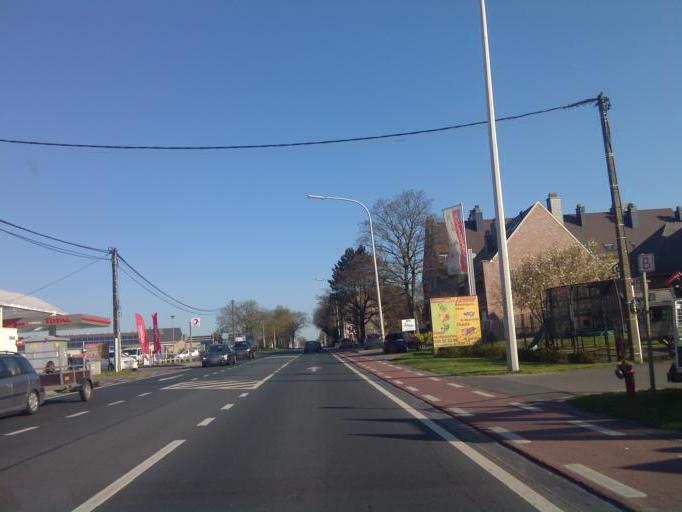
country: BE
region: Wallonia
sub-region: Province du Brabant Wallon
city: Chastre-Villeroux-Blanmont
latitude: 50.6448
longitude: 4.6456
